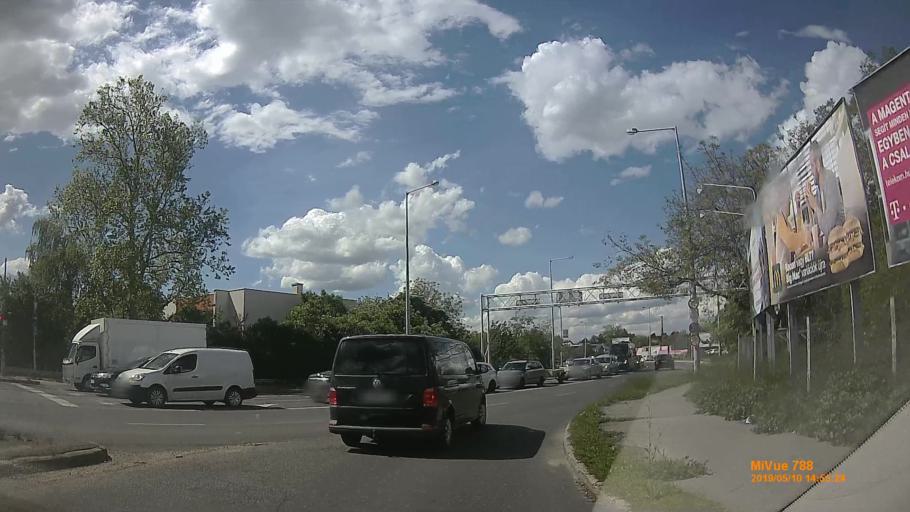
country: HU
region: Fejer
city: Szekesfehervar
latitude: 47.1951
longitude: 18.4458
